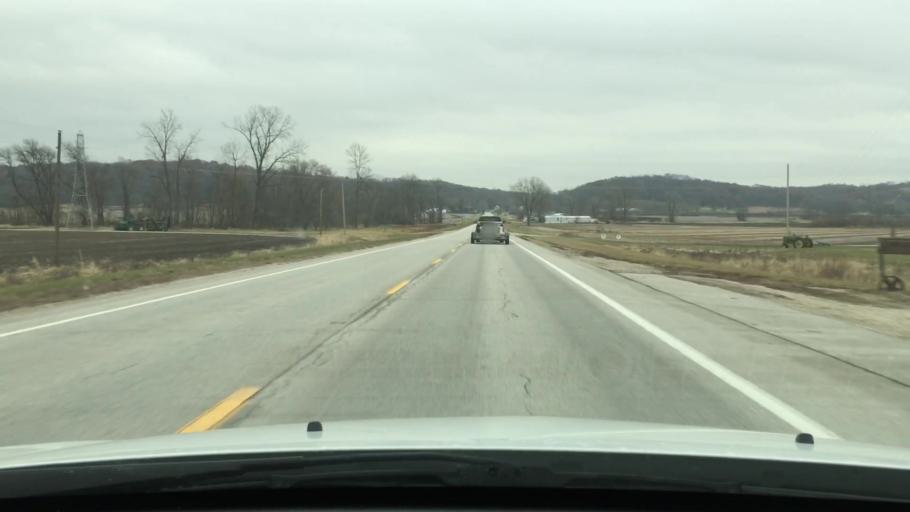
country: US
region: Missouri
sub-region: Pike County
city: Louisiana
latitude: 39.5068
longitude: -90.9832
